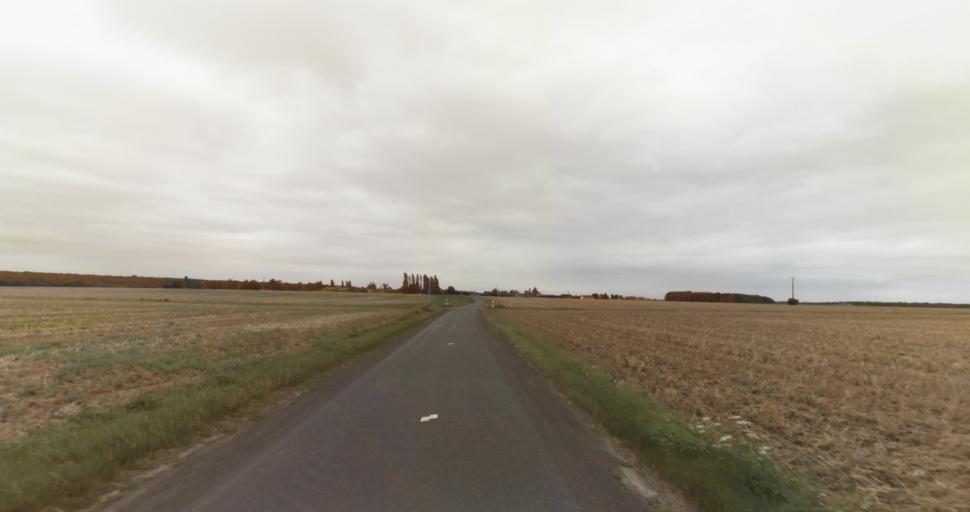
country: FR
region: Haute-Normandie
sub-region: Departement de l'Eure
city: La Couture-Boussey
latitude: 48.9186
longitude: 1.4039
